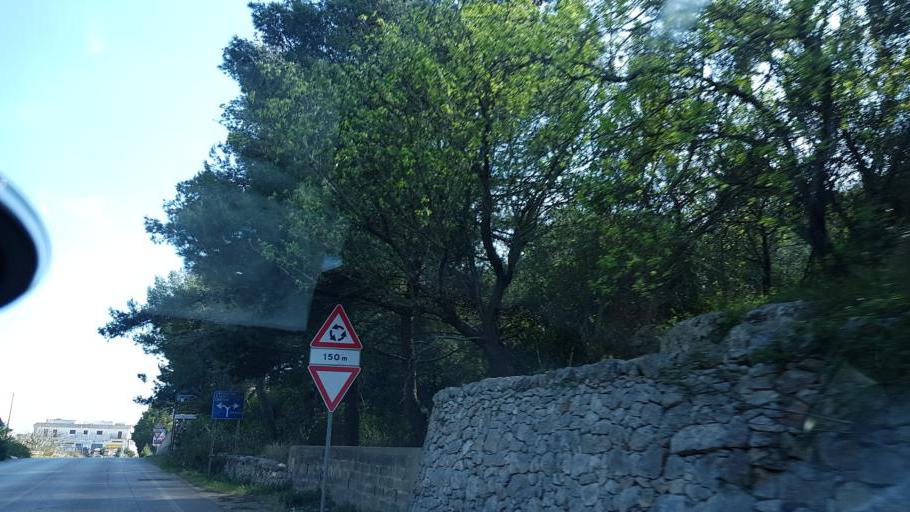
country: IT
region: Apulia
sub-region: Provincia di Brindisi
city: Ostuni
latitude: 40.7262
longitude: 17.5906
